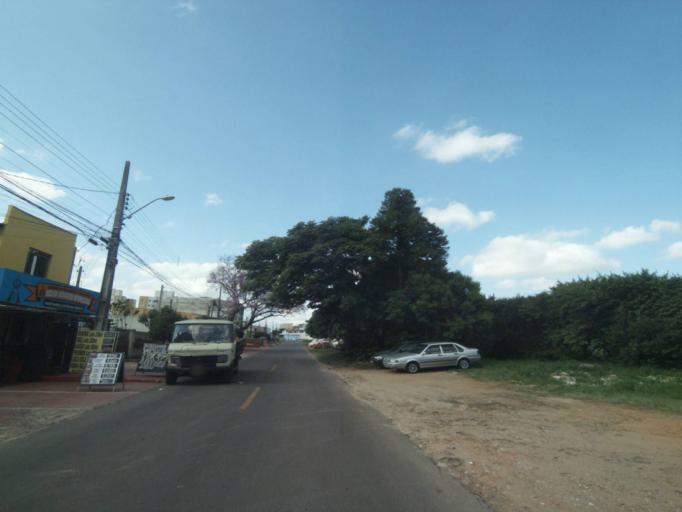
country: BR
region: Parana
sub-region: Curitiba
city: Curitiba
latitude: -25.4995
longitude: -49.3248
